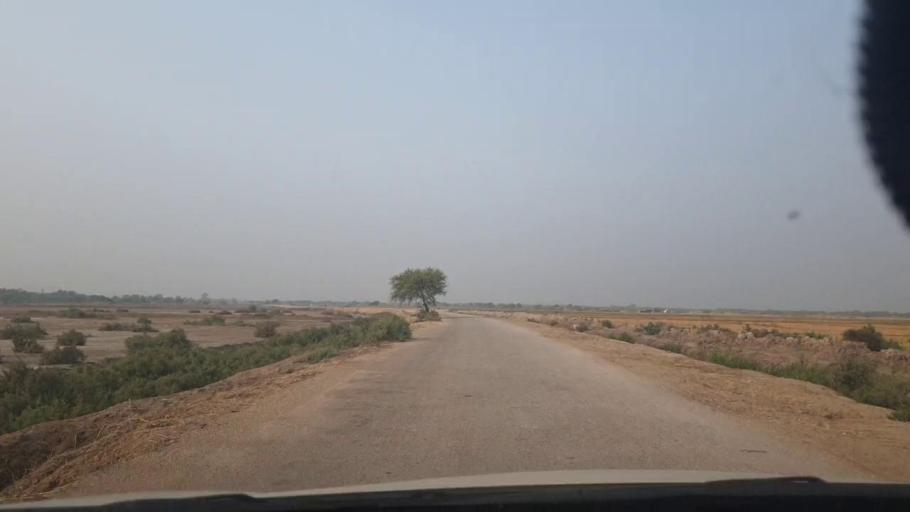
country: PK
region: Sindh
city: Bulri
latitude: 24.7885
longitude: 68.4190
